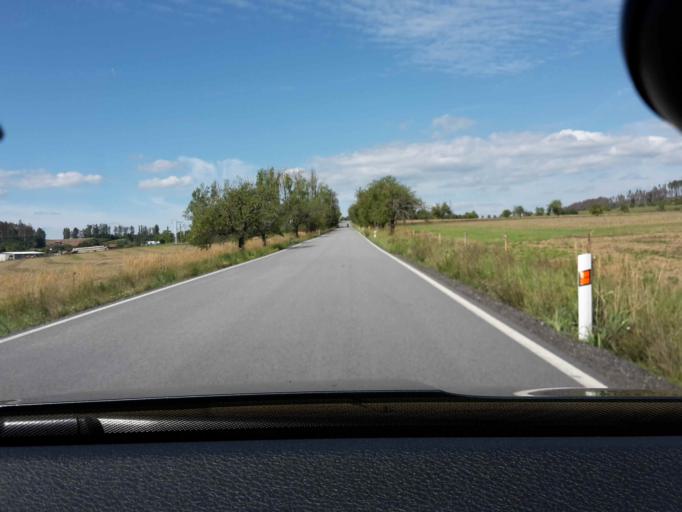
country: CZ
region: Vysocina
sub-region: Okres Jihlava
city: Telc
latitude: 49.1498
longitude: 15.5382
